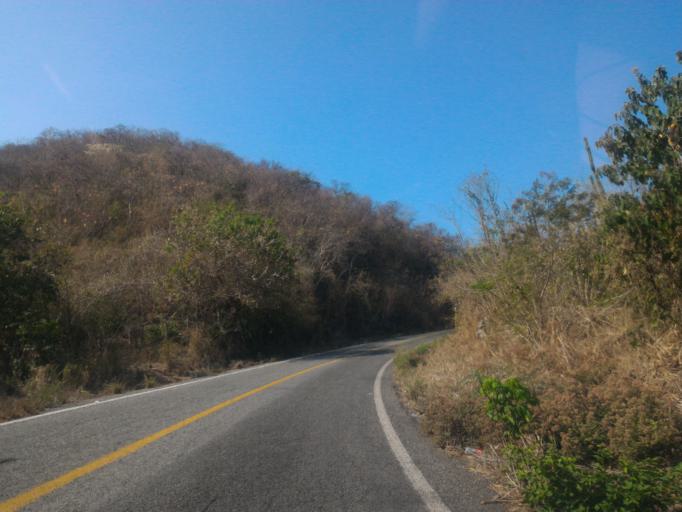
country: MX
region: Michoacan
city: Coahuayana Viejo
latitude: 18.4944
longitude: -103.5707
